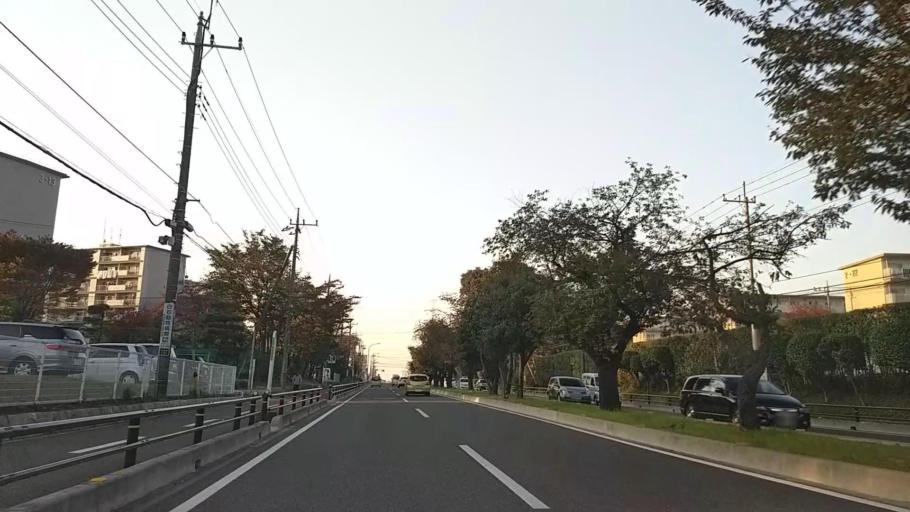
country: JP
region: Saitama
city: Sayama
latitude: 35.8572
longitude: 139.4328
